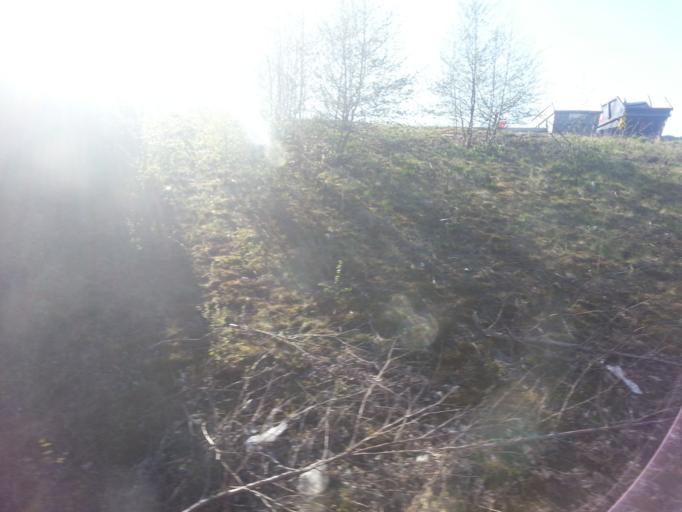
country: NO
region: Nord-Trondelag
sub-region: Stjordal
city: Stjordal
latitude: 63.4506
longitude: 10.9131
